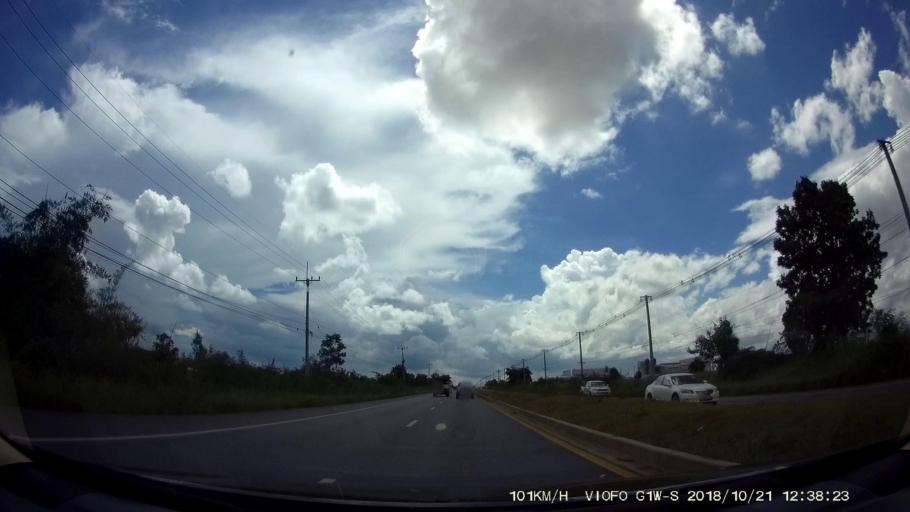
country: TH
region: Nakhon Ratchasima
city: Amphoe Sikhiu
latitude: 15.0550
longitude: 101.7064
